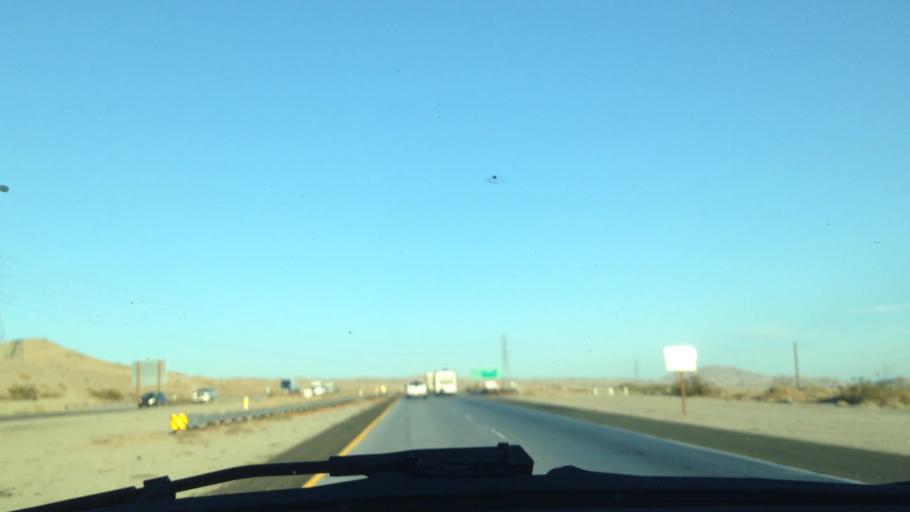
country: US
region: California
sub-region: Riverside County
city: Coachella
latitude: 33.7094
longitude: -116.1495
